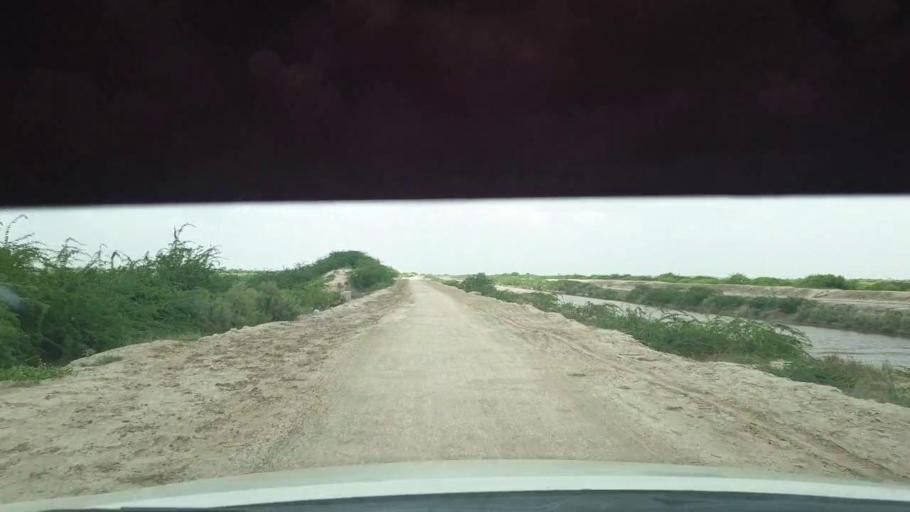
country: PK
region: Sindh
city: Kadhan
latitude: 24.5084
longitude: 69.1186
